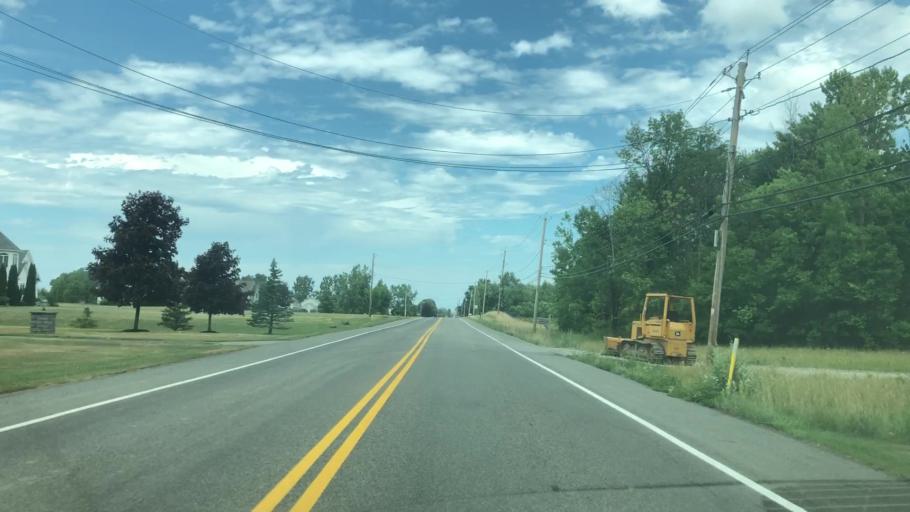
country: US
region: New York
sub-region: Monroe County
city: Webster
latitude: 43.1987
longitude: -77.4004
